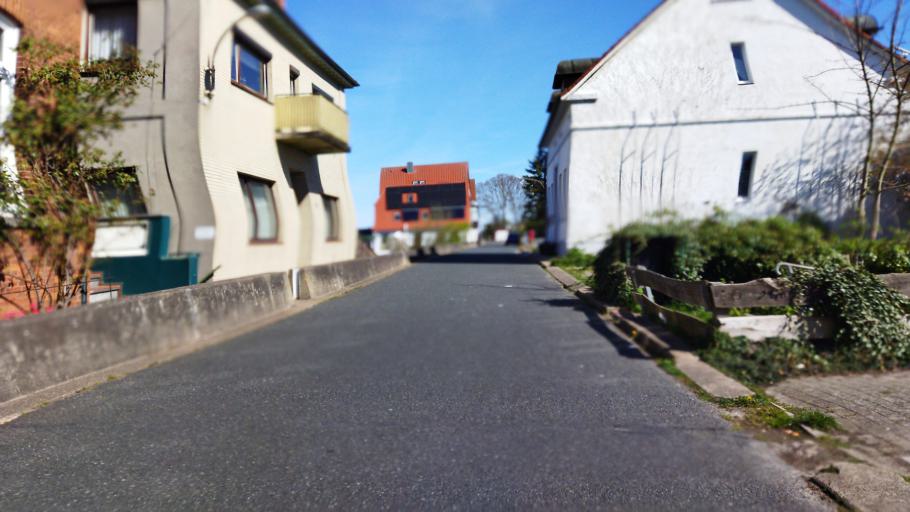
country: DE
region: Lower Saxony
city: Elsfleth
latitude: 53.2410
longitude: 8.4657
